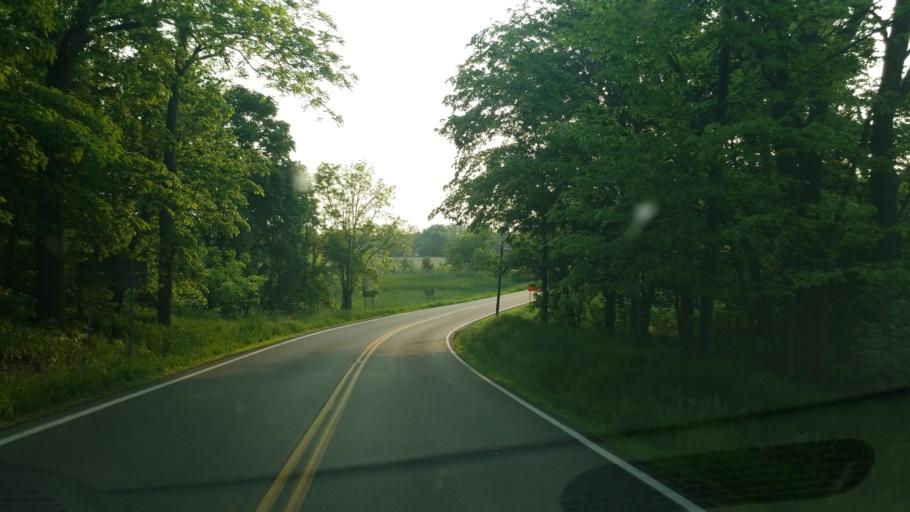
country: US
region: Ohio
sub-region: Ashland County
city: Ashland
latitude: 40.9217
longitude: -82.2832
